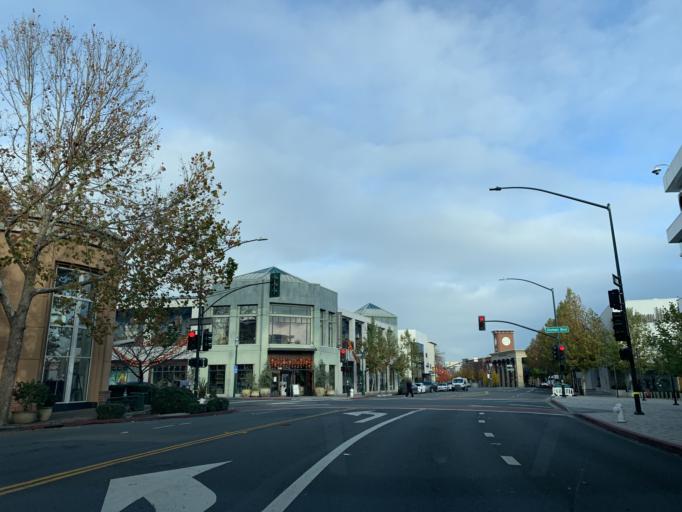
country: US
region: California
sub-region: Contra Costa County
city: Walnut Creek
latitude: 37.8960
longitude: -122.0599
